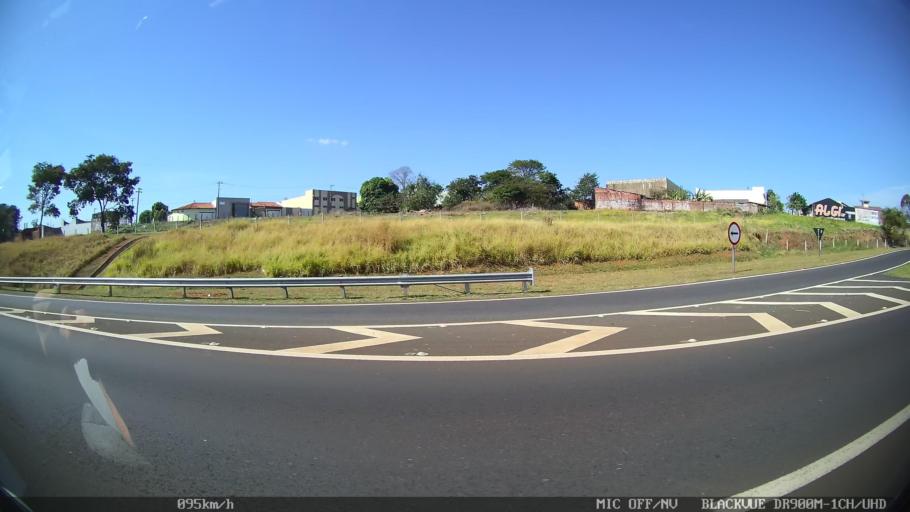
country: BR
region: Sao Paulo
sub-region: Franca
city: Franca
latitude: -20.5135
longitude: -47.4143
